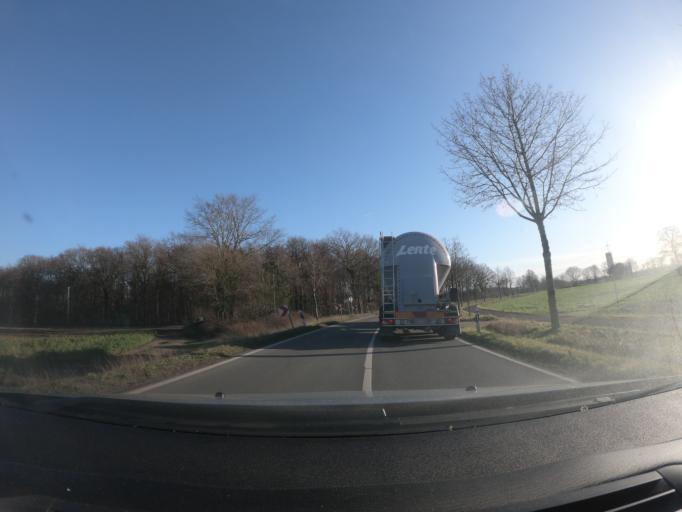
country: DE
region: North Rhine-Westphalia
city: Waltrop
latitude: 51.6548
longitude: 7.4231
